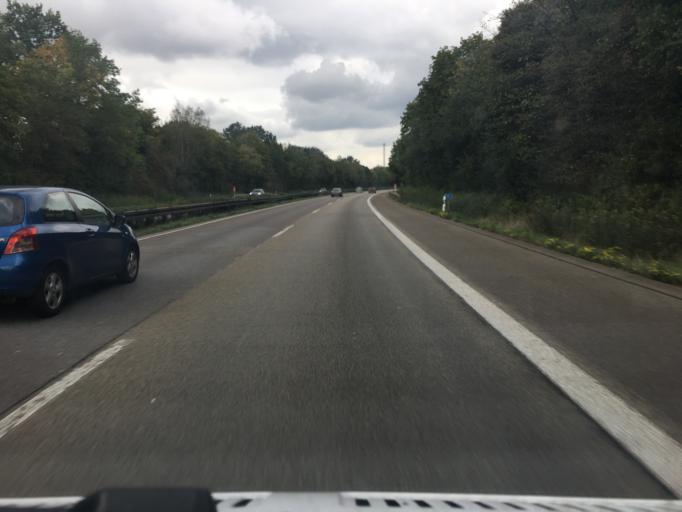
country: DE
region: North Rhine-Westphalia
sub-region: Regierungsbezirk Koln
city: Wahn-Heide
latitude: 50.8275
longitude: 7.0967
